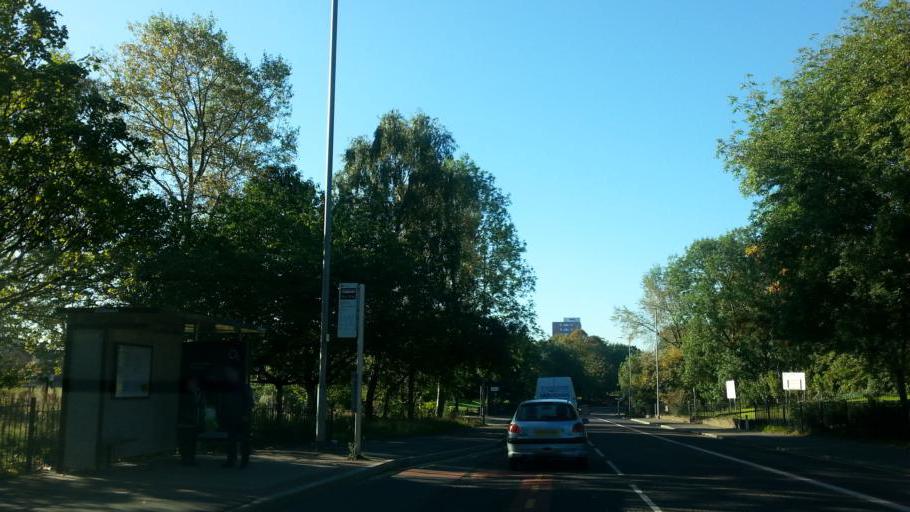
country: GB
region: England
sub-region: Manchester
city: Cheetham Hill
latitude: 53.4986
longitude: -2.2202
